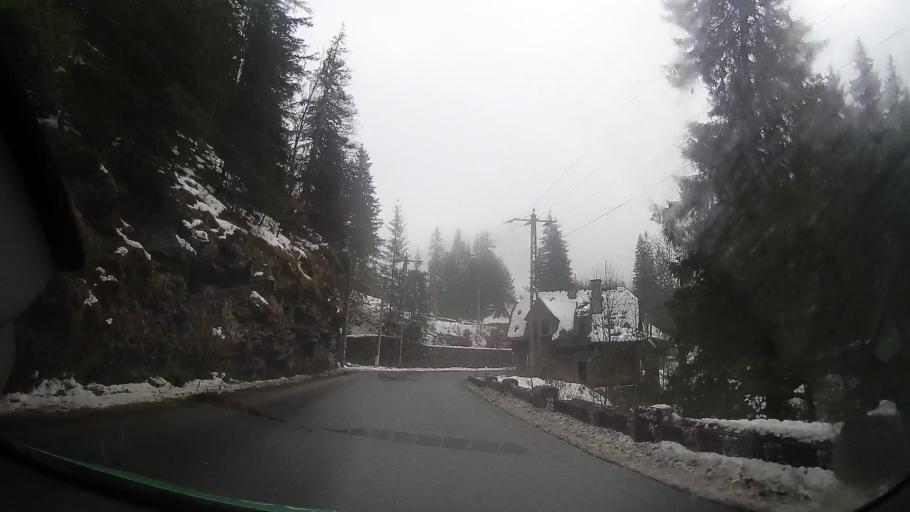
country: RO
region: Neamt
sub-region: Comuna Bicaz Chei
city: Bicaz Chei
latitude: 46.7981
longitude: 25.8018
